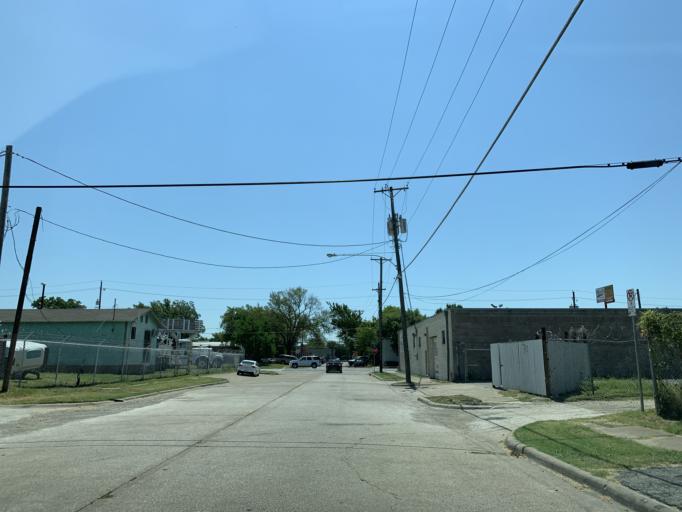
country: US
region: Texas
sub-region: Dallas County
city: Dallas
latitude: 32.7882
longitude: -96.7724
